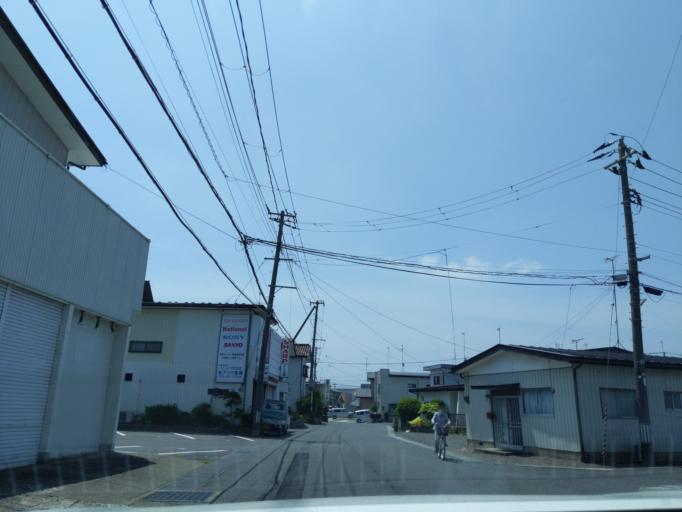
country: JP
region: Fukushima
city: Koriyama
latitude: 37.3711
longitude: 140.3571
